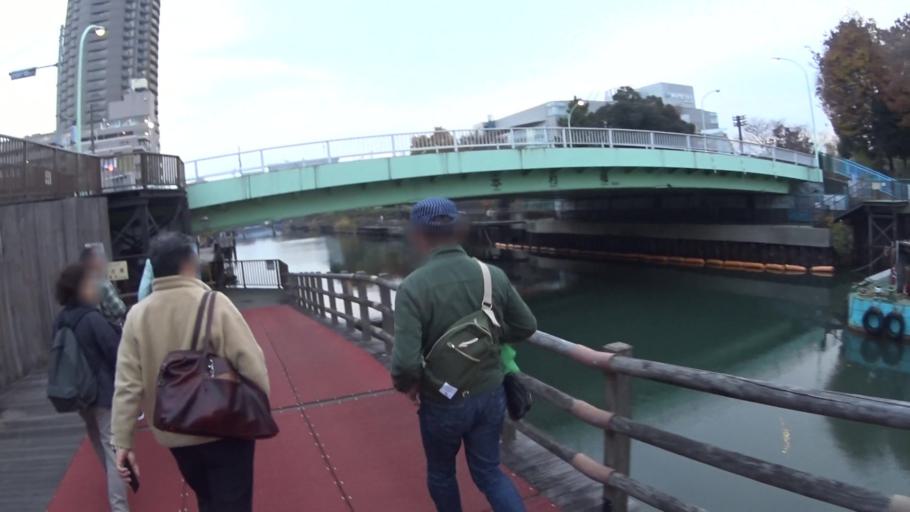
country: JP
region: Tokyo
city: Urayasu
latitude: 35.6895
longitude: 139.8204
